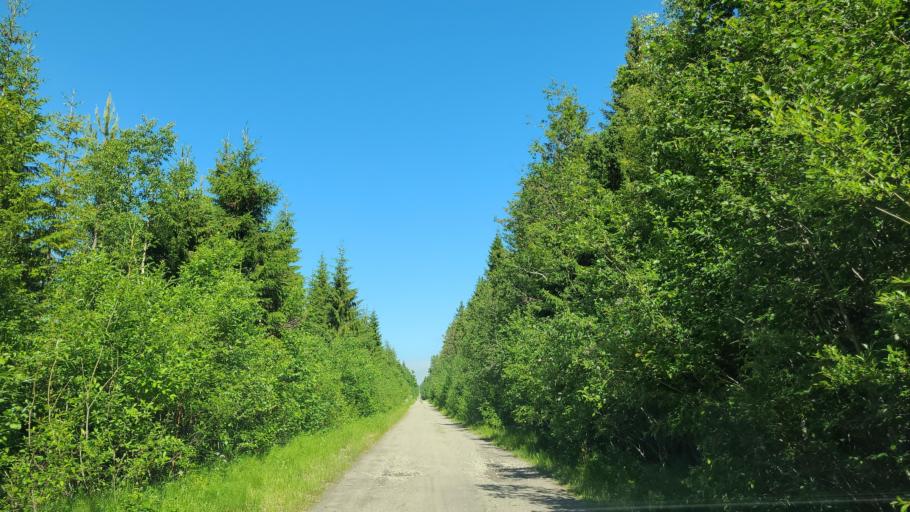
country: SE
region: Vaesternorrland
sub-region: OErnskoeldsviks Kommun
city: Husum
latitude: 63.4193
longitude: 19.2225
